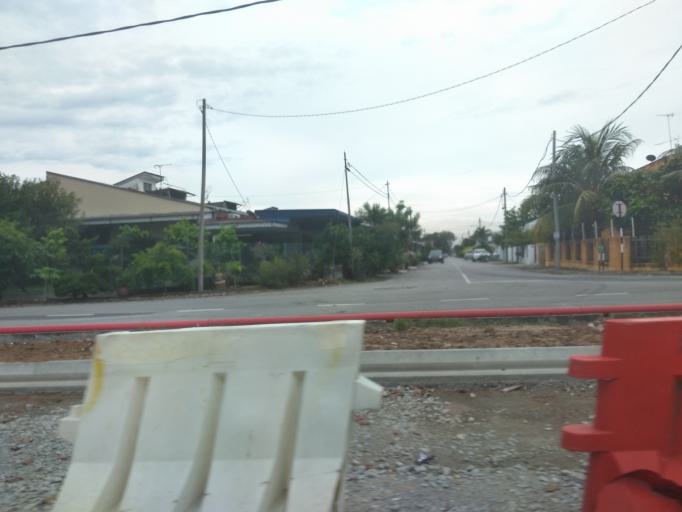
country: MY
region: Penang
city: Bukit Mertajam
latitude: 5.3331
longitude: 100.4821
